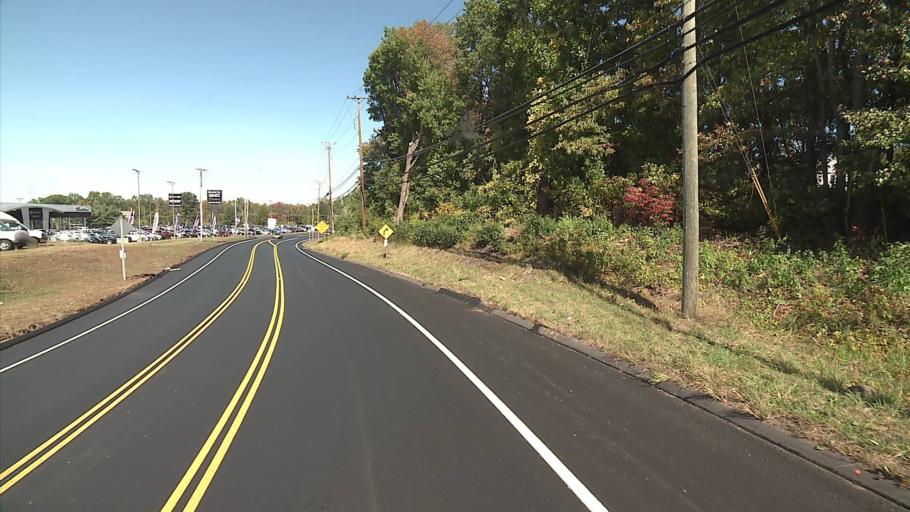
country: US
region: Connecticut
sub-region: Tolland County
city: Rockville
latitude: 41.8617
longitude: -72.4815
